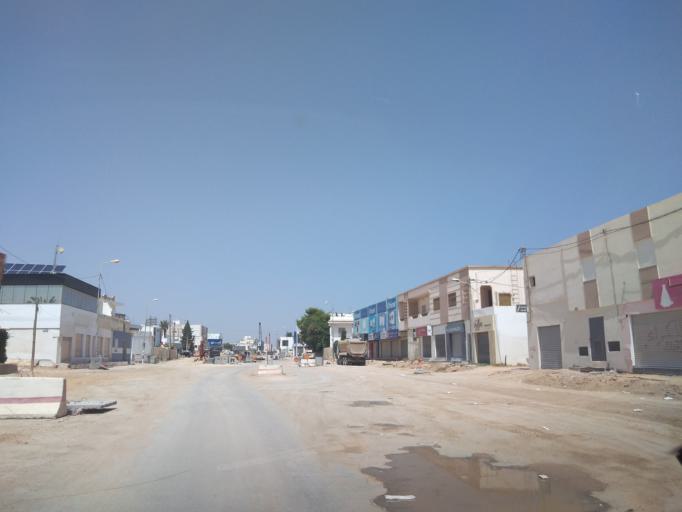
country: TN
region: Safaqis
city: Sfax
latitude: 34.7492
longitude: 10.7287
